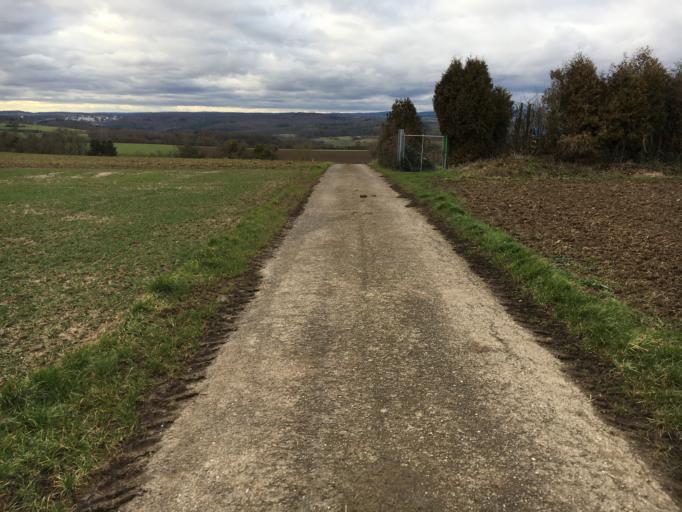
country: DE
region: Baden-Wuerttemberg
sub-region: Karlsruhe Region
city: Mosbach
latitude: 49.3757
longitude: 9.2005
